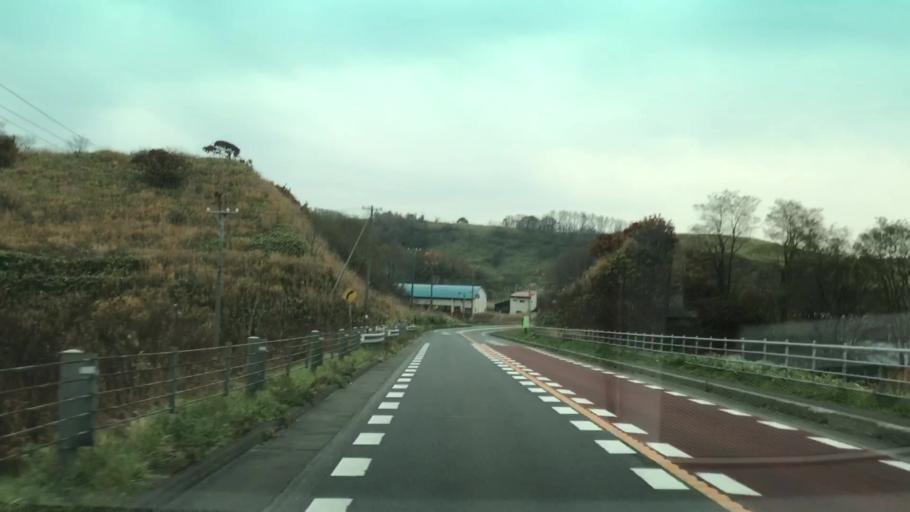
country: JP
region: Hokkaido
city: Ishikari
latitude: 43.3575
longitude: 141.4297
